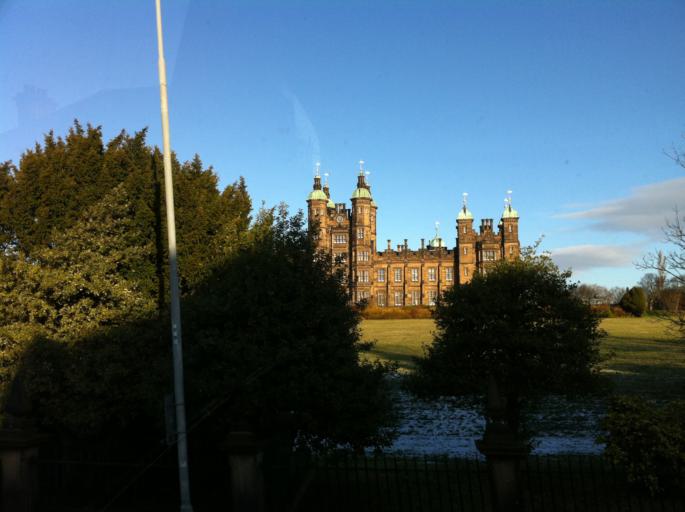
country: GB
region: Scotland
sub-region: Edinburgh
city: Edinburgh
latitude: 55.9459
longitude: -3.2252
